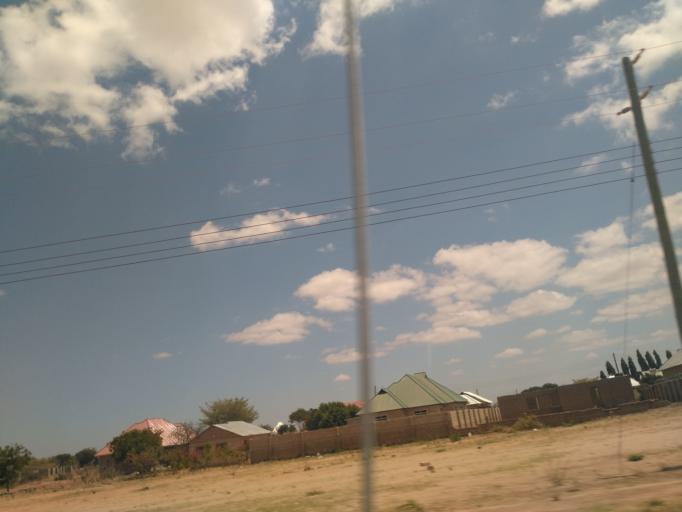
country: TZ
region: Dodoma
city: Kisasa
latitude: -6.1654
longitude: 35.7919
